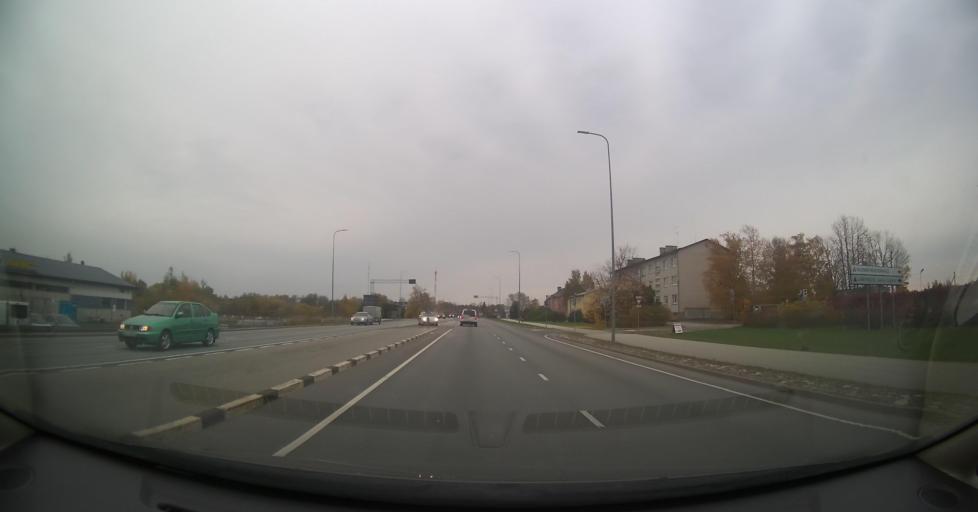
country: EE
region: Laeaene
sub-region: Ridala Parish
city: Uuemoisa
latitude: 58.9395
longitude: 23.5741
